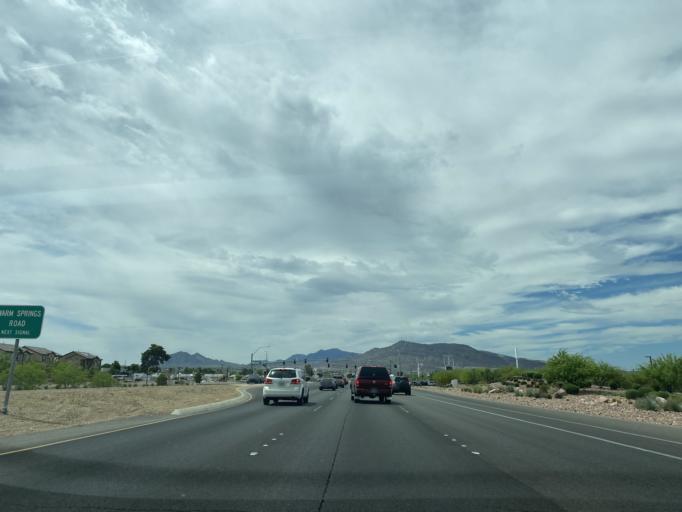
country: US
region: Nevada
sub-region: Clark County
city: Henderson
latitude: 36.0523
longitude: -114.9700
